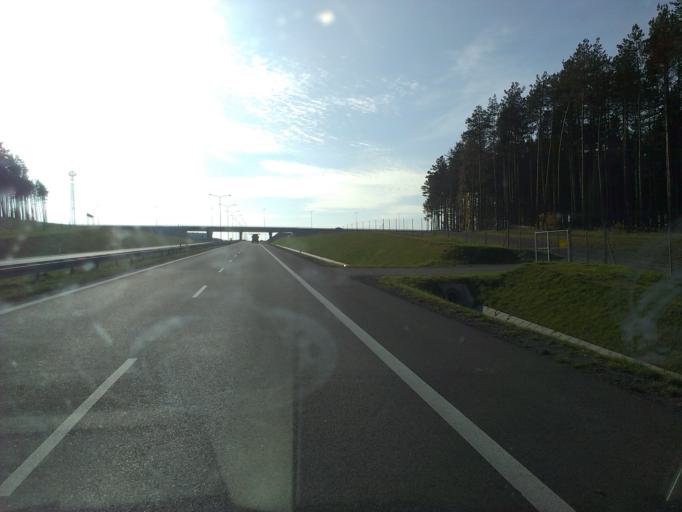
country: PL
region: Lubusz
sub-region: Powiat swiebodzinski
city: Swiebodzin
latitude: 52.3265
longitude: 15.5535
